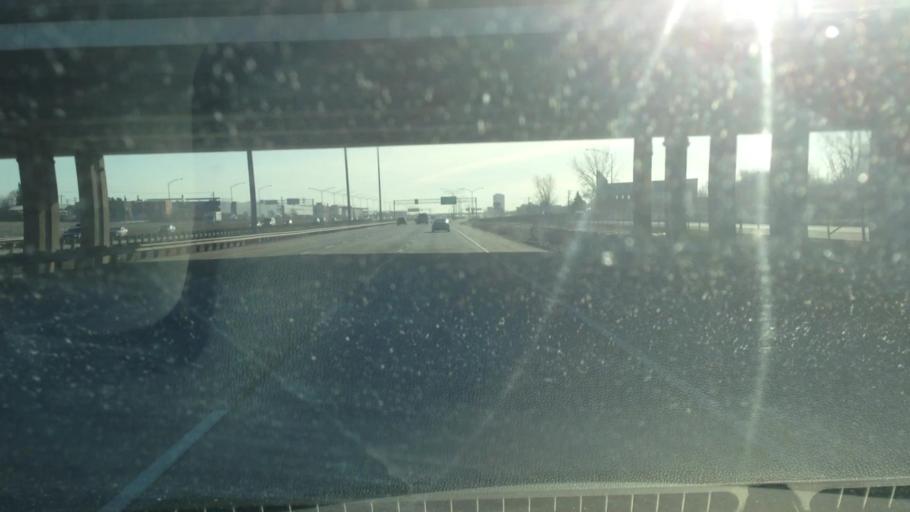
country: CA
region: Quebec
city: Dollard-Des Ormeaux
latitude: 45.5418
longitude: -73.7949
